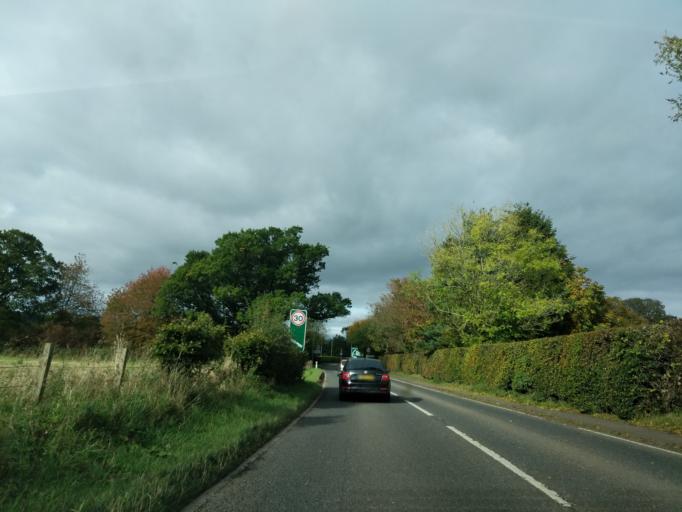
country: GB
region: Scotland
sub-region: Dumfries and Galloway
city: Thornhill
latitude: 55.2600
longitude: -3.7781
